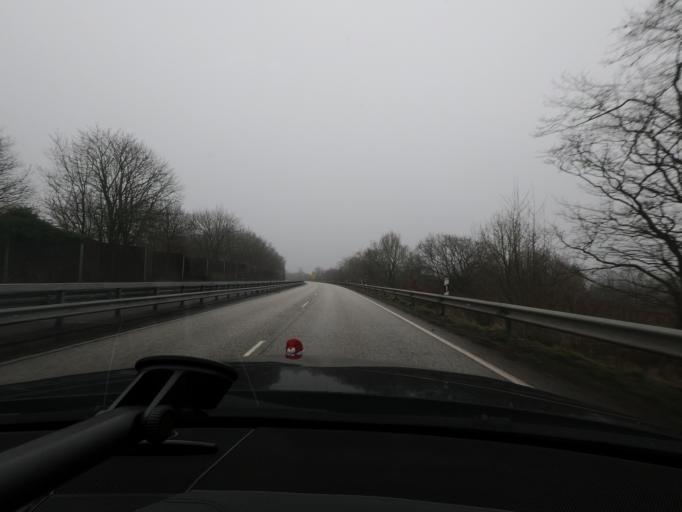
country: DE
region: Schleswig-Holstein
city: Harrislee
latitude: 54.7866
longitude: 9.4030
